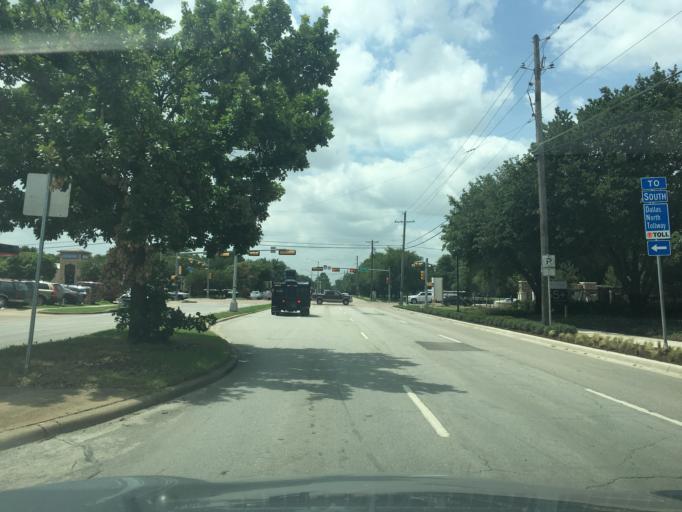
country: US
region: Texas
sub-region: Dallas County
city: Addison
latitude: 32.9104
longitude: -96.8185
